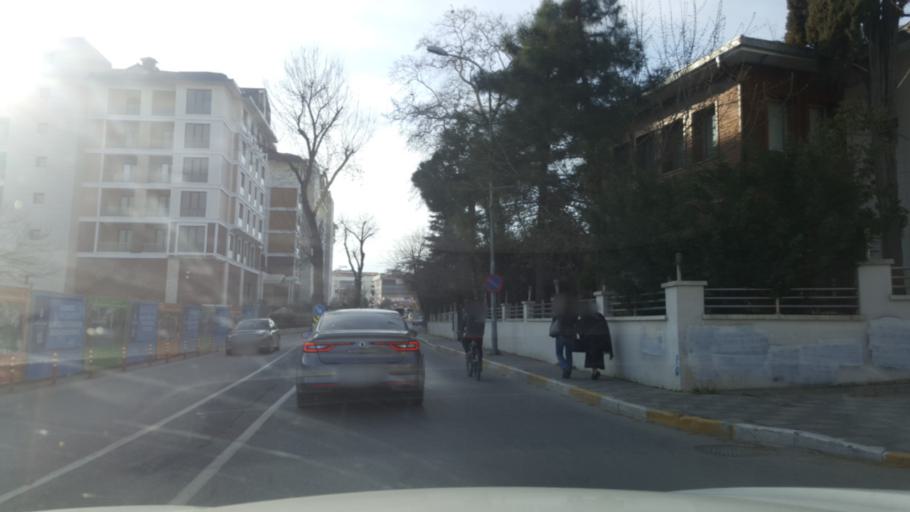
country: TR
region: Istanbul
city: Icmeler
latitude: 40.8180
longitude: 29.3010
